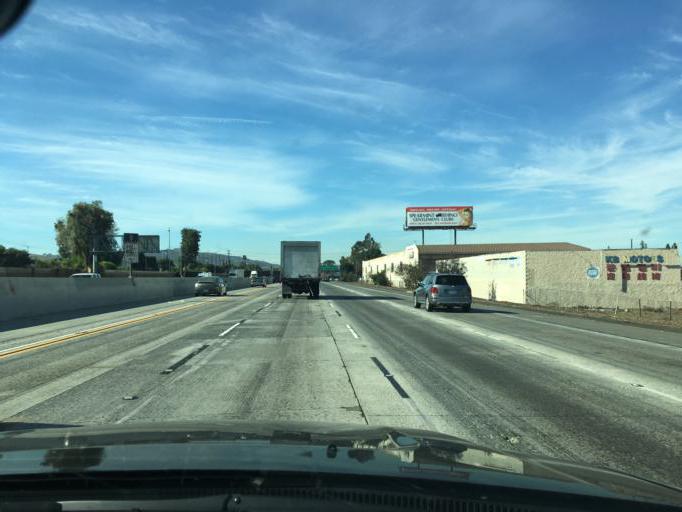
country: US
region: California
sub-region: Los Angeles County
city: Walnut
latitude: 33.9948
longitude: -117.8806
